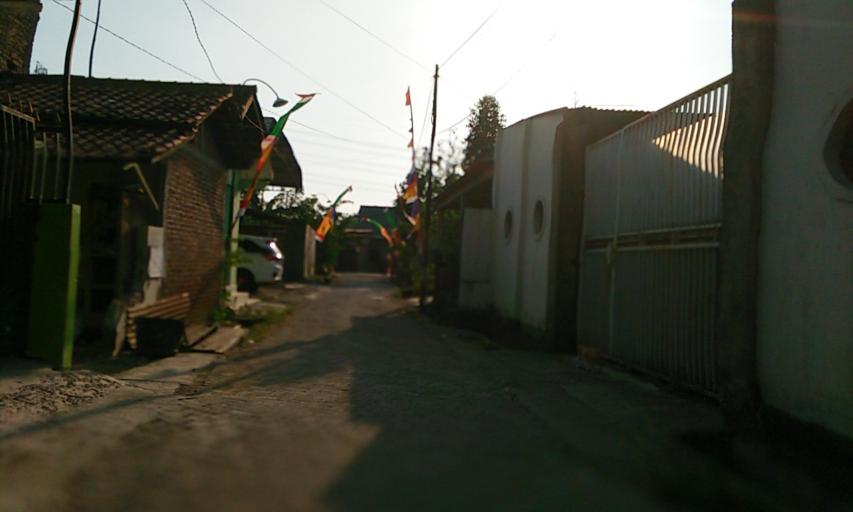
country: ID
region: Central Java
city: Mranggen
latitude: -7.0150
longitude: 110.4897
